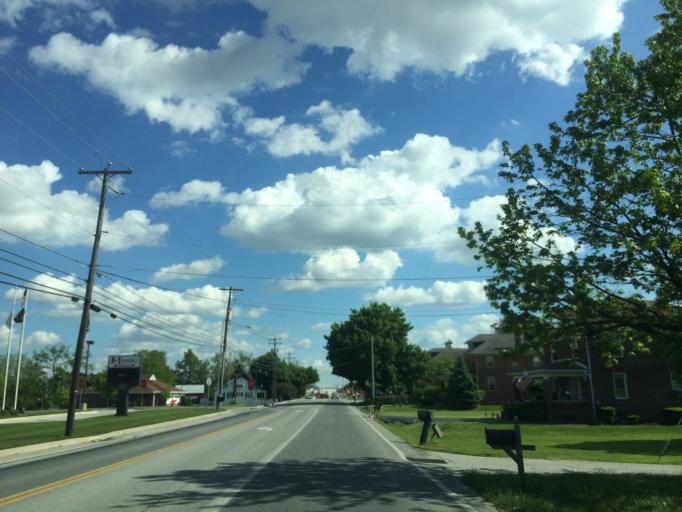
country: US
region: Pennsylvania
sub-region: York County
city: Parkville
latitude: 39.7662
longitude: -76.9607
